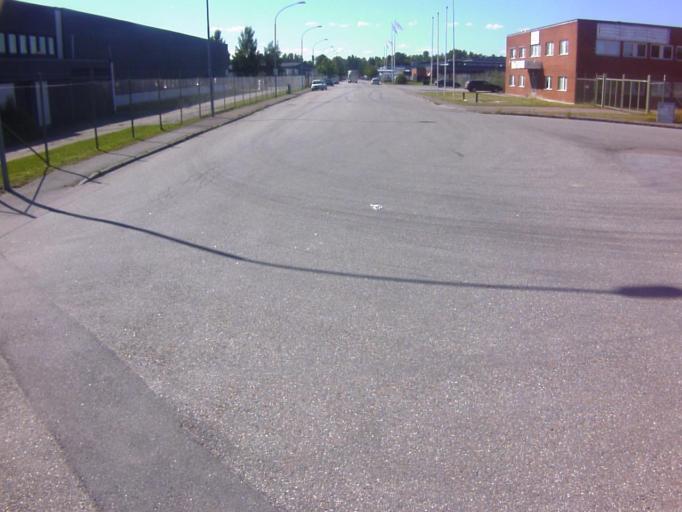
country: SE
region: Soedermanland
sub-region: Eskilstuna Kommun
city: Eskilstuna
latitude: 59.3883
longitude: 16.4944
